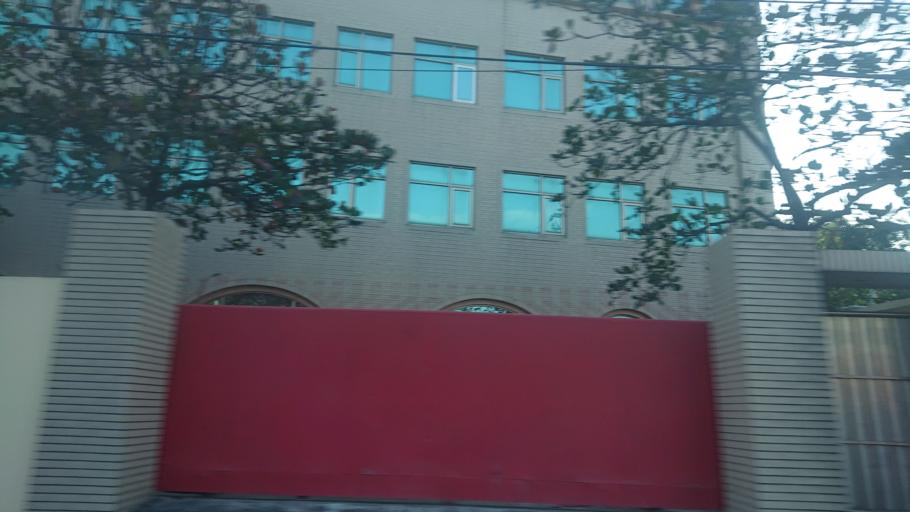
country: TW
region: Taiwan
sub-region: Tainan
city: Tainan
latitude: 23.0758
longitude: 120.2129
